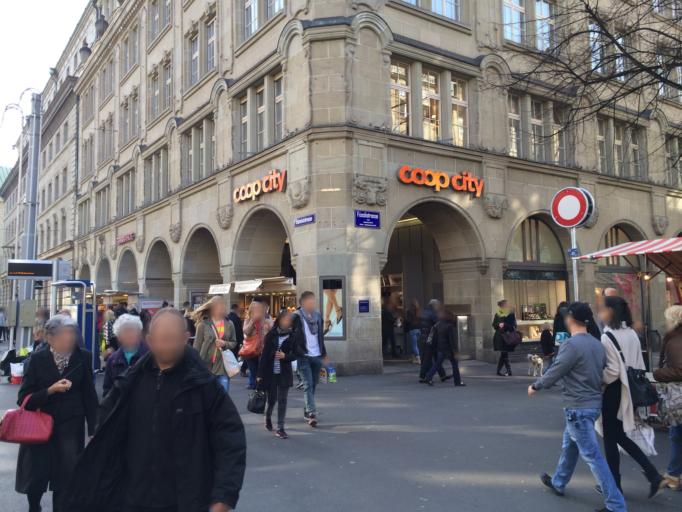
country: CH
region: Zurich
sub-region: Bezirk Zuerich
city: Zuerich (Kreis 1) / Lindenhof
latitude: 47.3731
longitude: 8.5383
